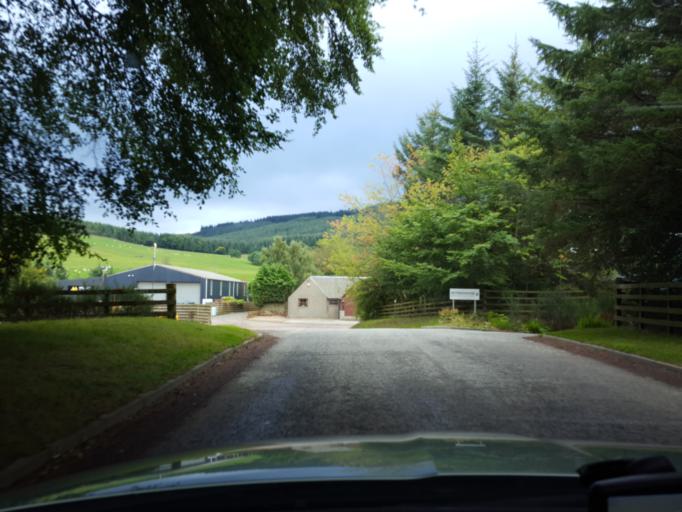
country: GB
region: Scotland
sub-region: Aberdeenshire
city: Banchory
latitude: 57.1468
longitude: -2.5021
